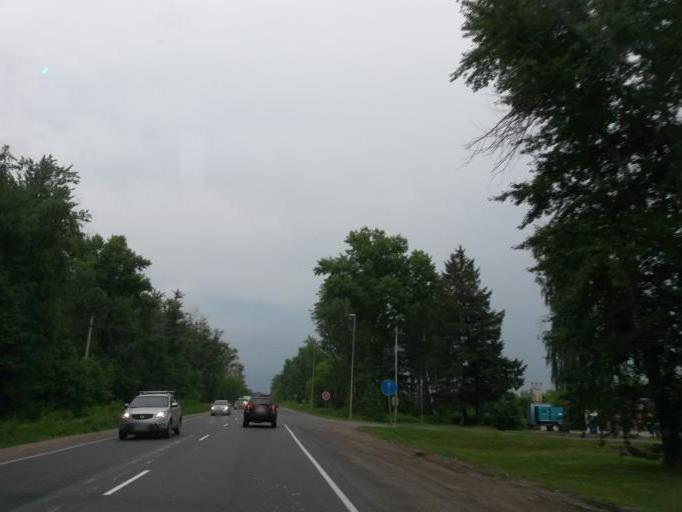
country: RU
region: Moskovskaya
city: Yam
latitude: 55.4562
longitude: 37.6809
